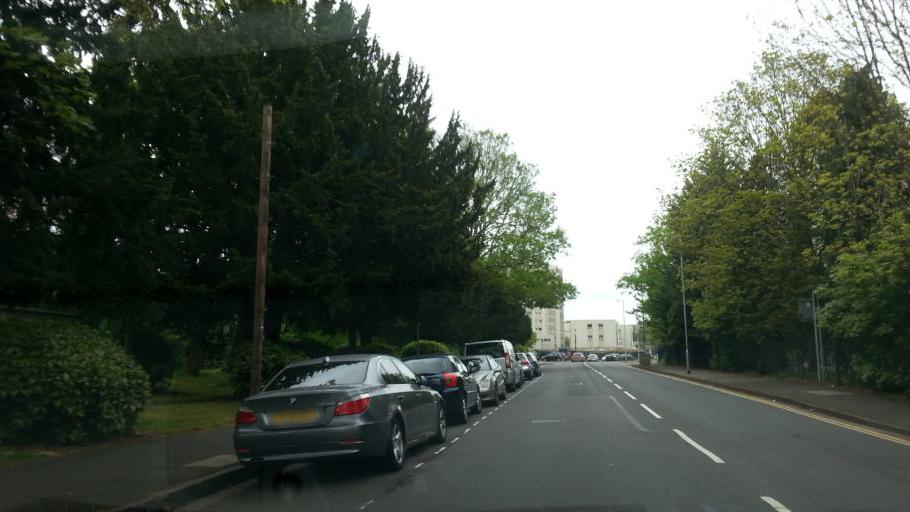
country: GB
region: England
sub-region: Peterborough
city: Peterborough
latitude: 52.5718
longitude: -0.2371
